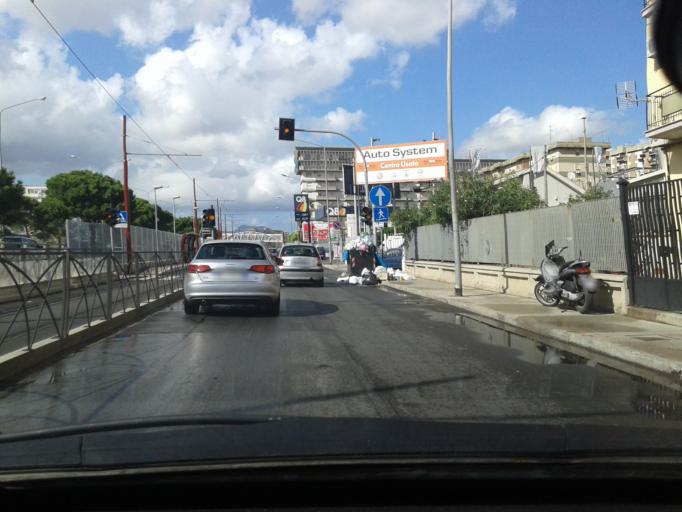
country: IT
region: Sicily
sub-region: Palermo
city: Palermo
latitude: 38.1132
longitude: 13.3297
